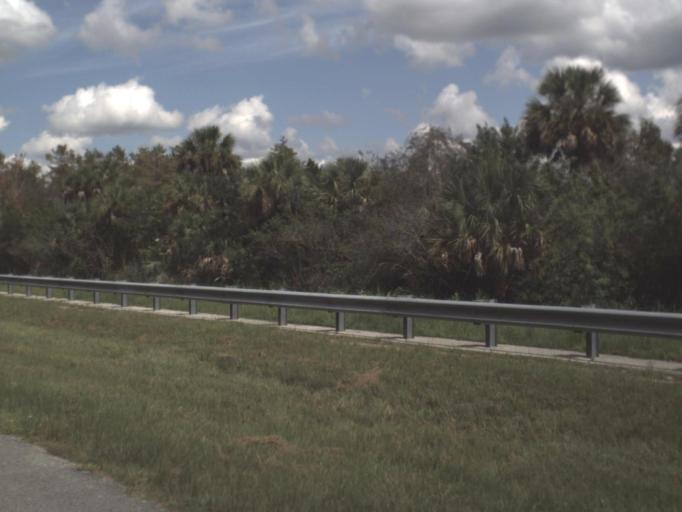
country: US
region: Florida
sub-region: Collier County
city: Lely Resort
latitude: 26.0018
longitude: -81.3467
